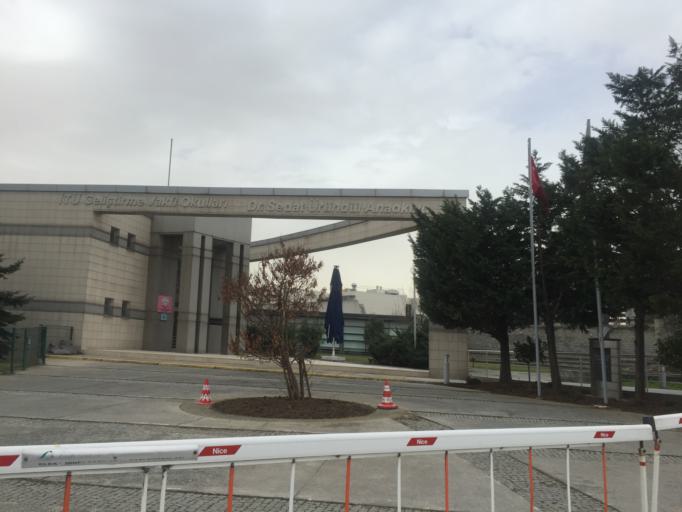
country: TR
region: Istanbul
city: Sisli
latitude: 41.1065
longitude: 29.0276
